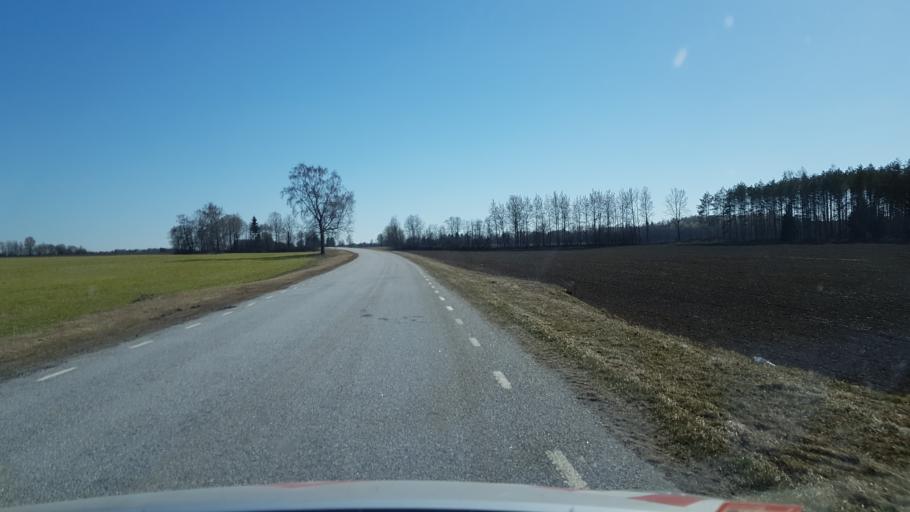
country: EE
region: Jaervamaa
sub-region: Koeru vald
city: Koeru
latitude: 59.0253
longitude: 26.0886
